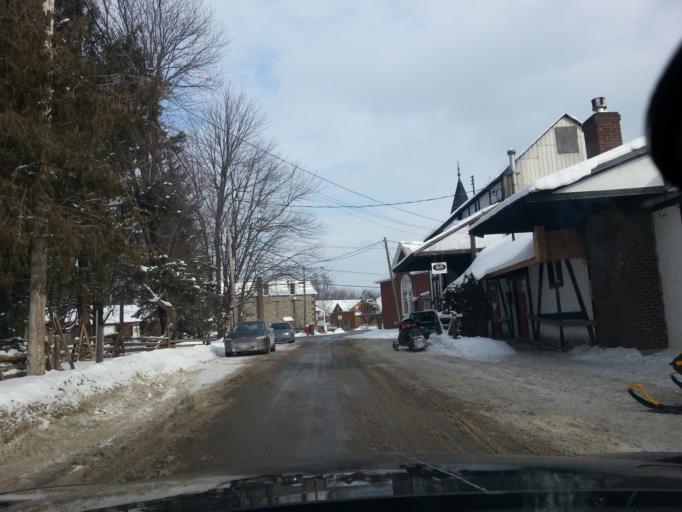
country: CA
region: Ontario
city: Carleton Place
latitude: 45.1567
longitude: -76.0337
